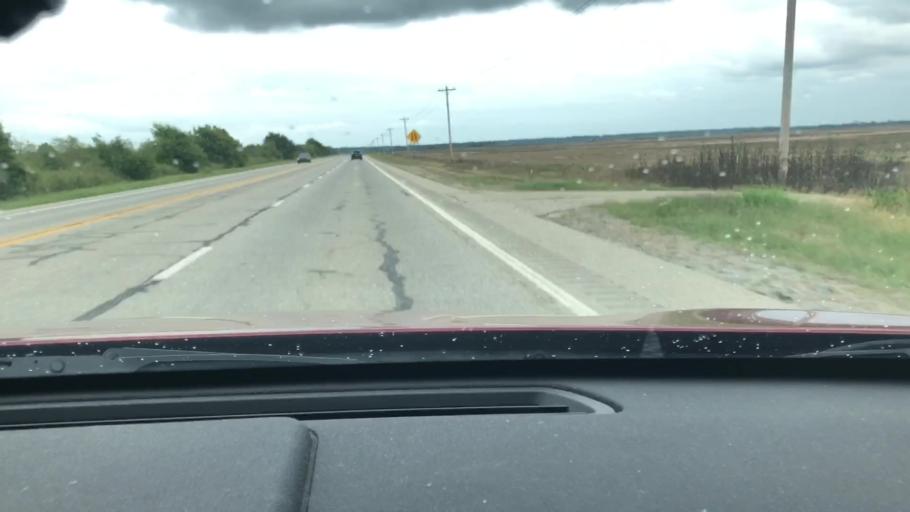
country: US
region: Arkansas
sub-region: Lafayette County
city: Lewisville
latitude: 33.4120
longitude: -93.7812
